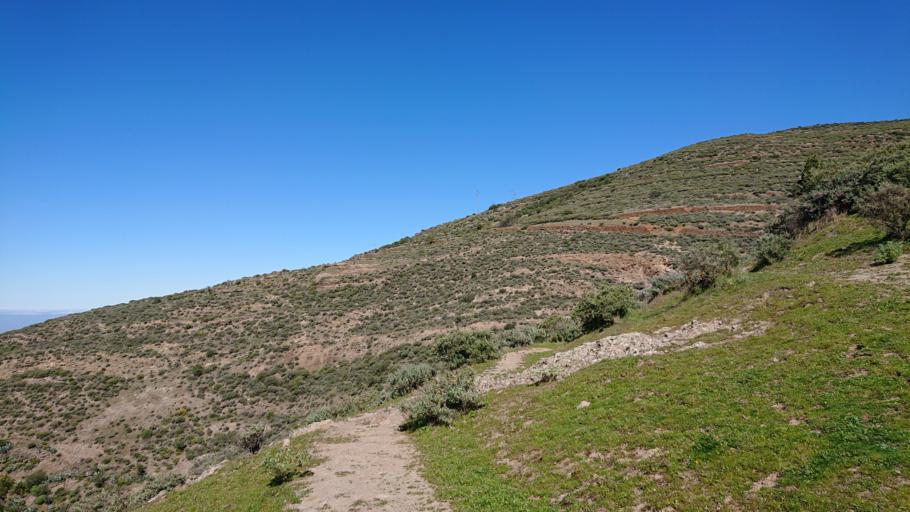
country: ES
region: Canary Islands
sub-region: Provincia de Las Palmas
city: Artenara
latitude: 28.0200
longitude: -15.6415
